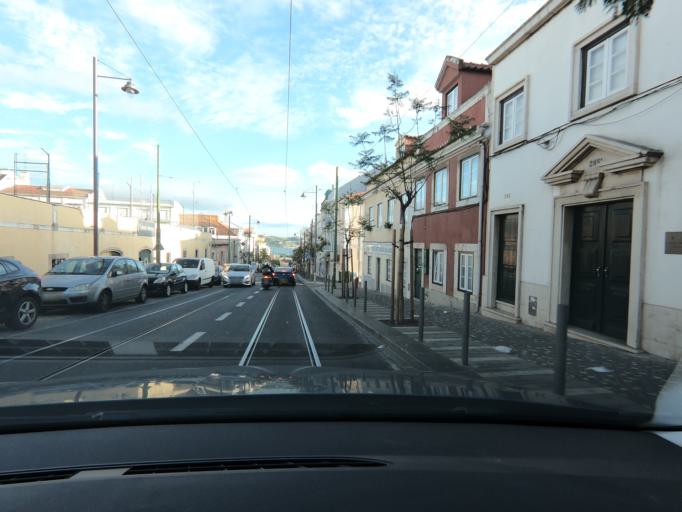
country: PT
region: Lisbon
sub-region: Oeiras
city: Alges
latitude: 38.7053
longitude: -9.1993
